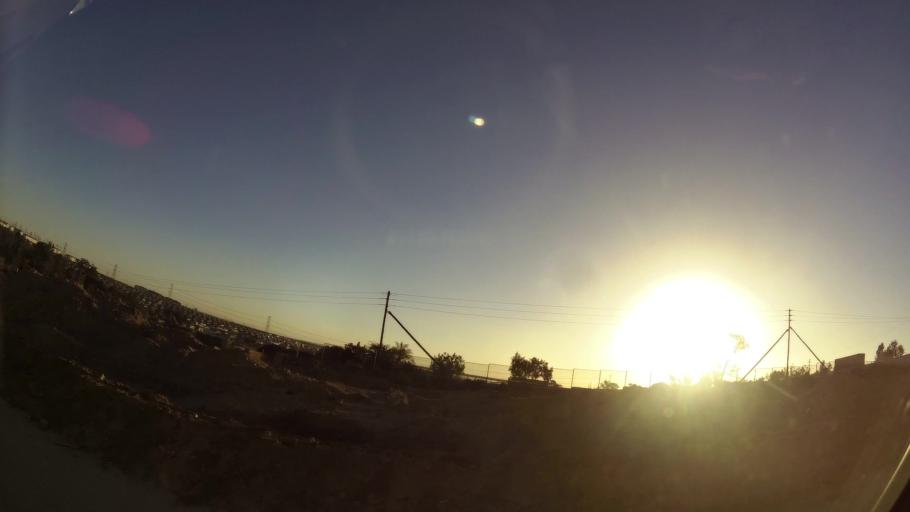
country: ZA
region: Gauteng
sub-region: City of Johannesburg Metropolitan Municipality
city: Diepsloot
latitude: -25.9563
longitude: 28.0176
